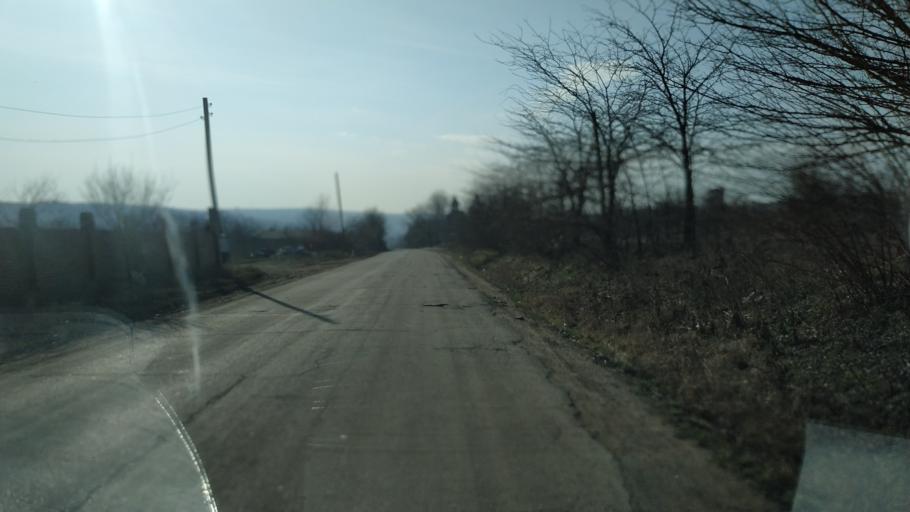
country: MD
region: Chisinau
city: Singera
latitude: 46.8424
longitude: 29.0259
